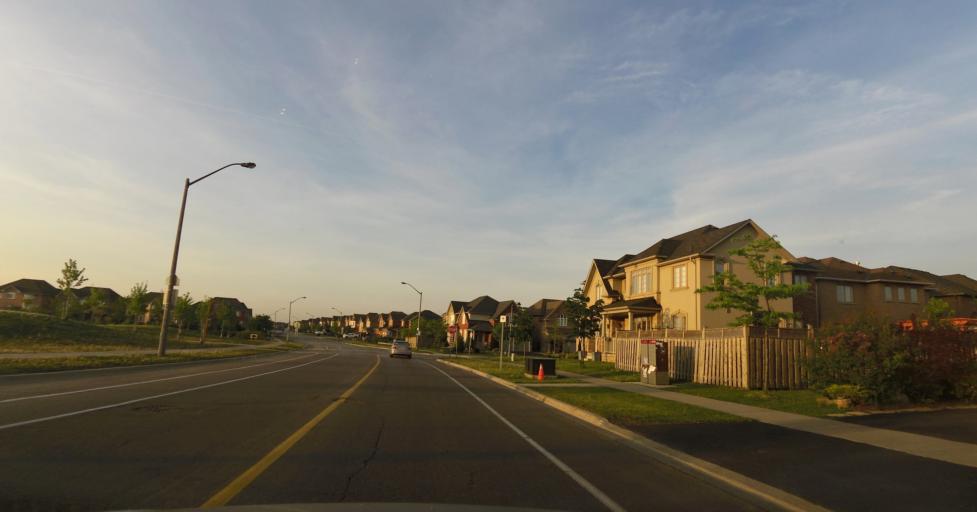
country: CA
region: Ontario
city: Oakville
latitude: 43.4429
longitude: -79.7622
